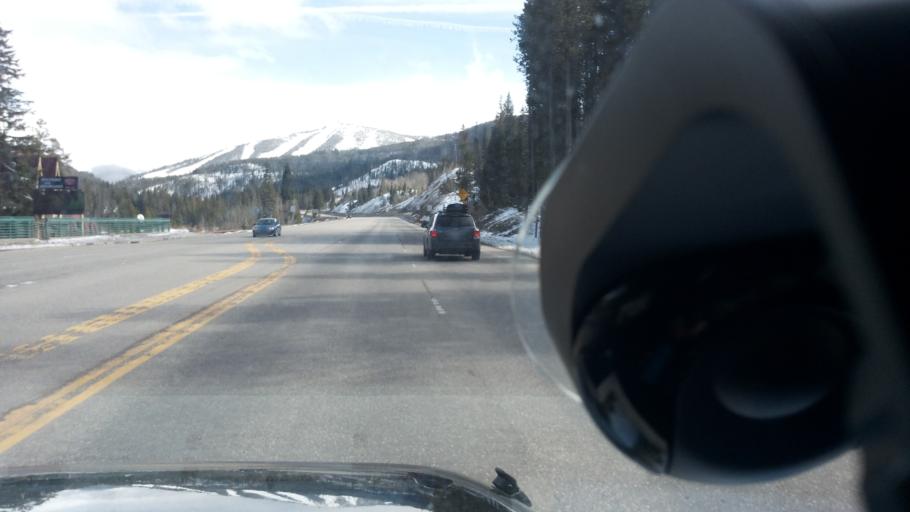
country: US
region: Colorado
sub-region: Grand County
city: Fraser
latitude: 39.9139
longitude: -105.7824
